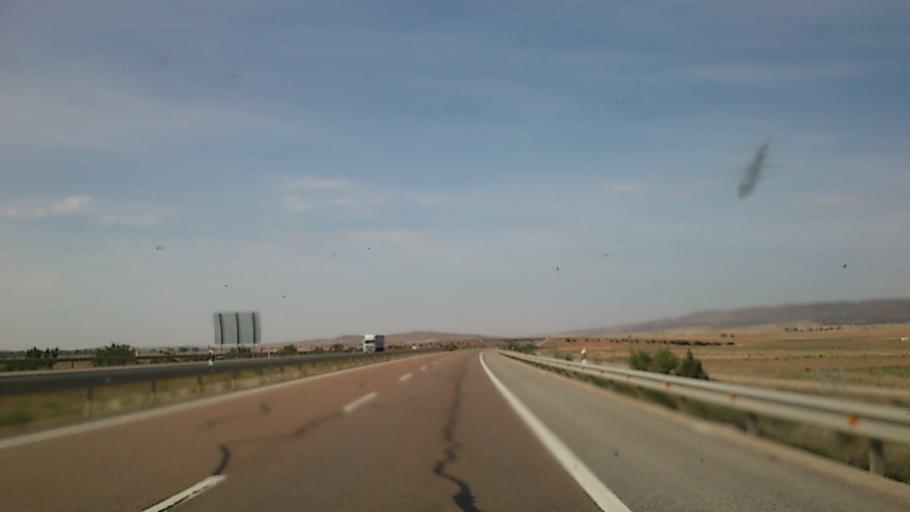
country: ES
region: Aragon
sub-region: Provincia de Teruel
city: Santa Eulalia
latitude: 40.5818
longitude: -1.2842
